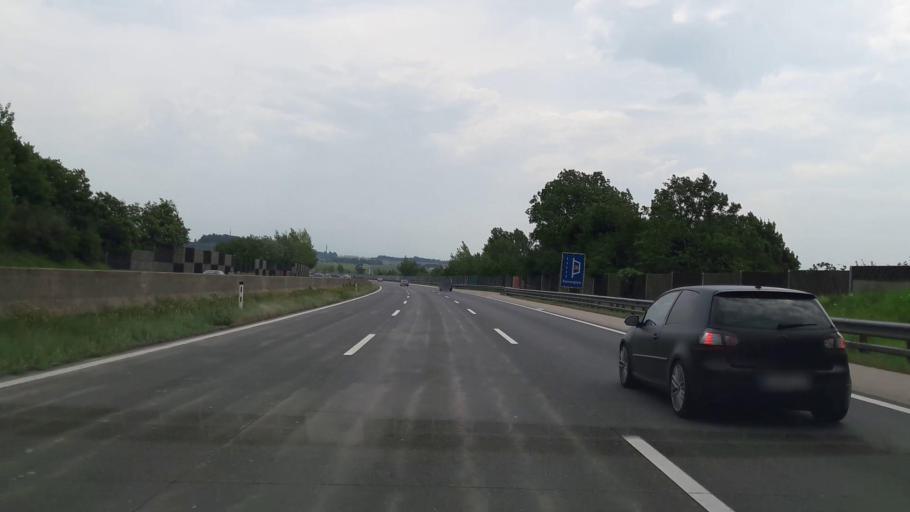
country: AT
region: Lower Austria
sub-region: Politischer Bezirk Amstetten
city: Sankt Valentin
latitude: 48.1509
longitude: 14.5618
